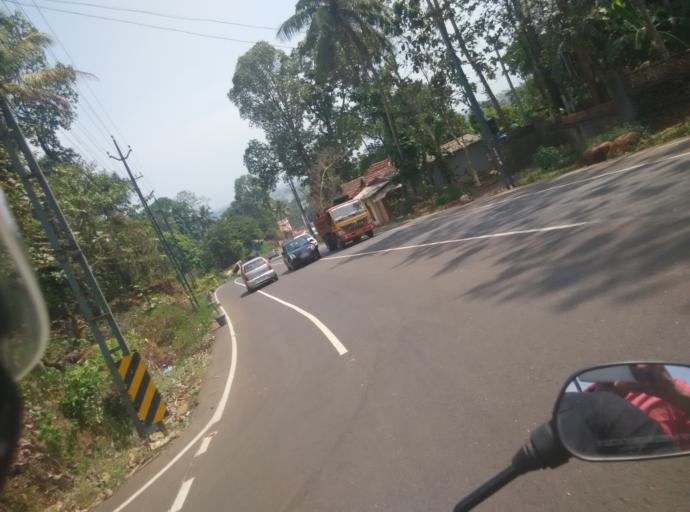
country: IN
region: Kerala
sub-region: Kottayam
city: Lalam
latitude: 9.7150
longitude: 76.6796
